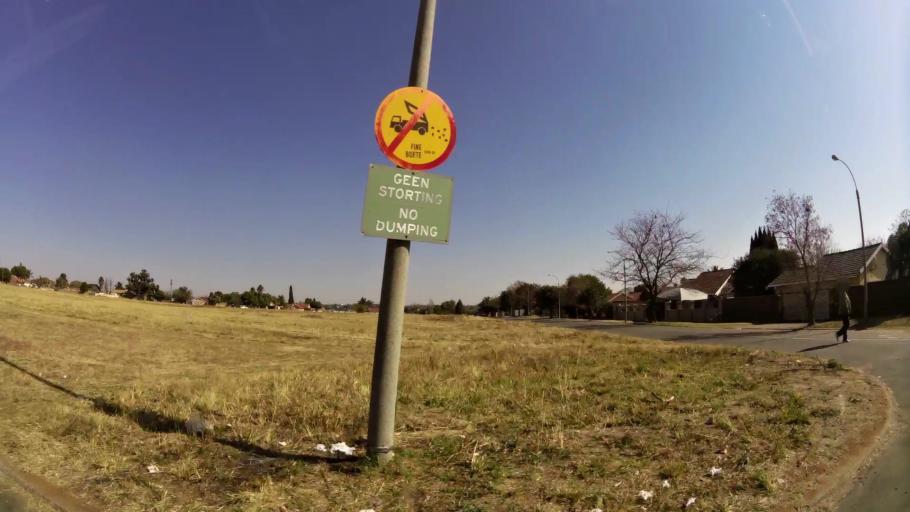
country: ZA
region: Gauteng
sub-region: Ekurhuleni Metropolitan Municipality
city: Tembisa
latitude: -26.0469
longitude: 28.2300
